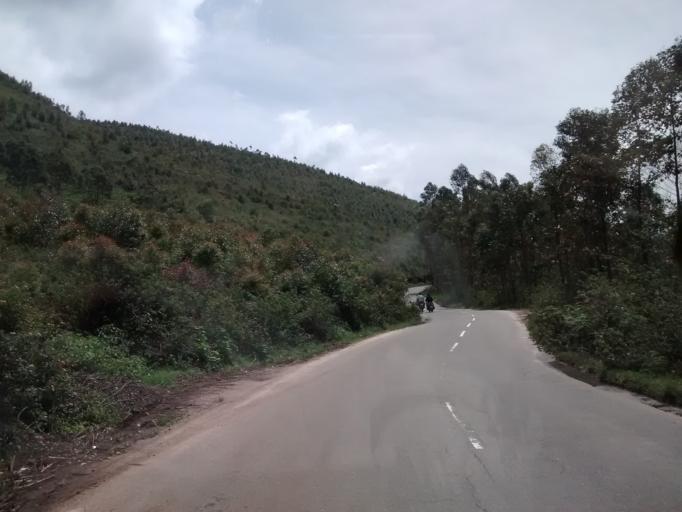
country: IN
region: Kerala
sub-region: Idukki
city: Munnar
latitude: 10.0984
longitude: 77.1047
